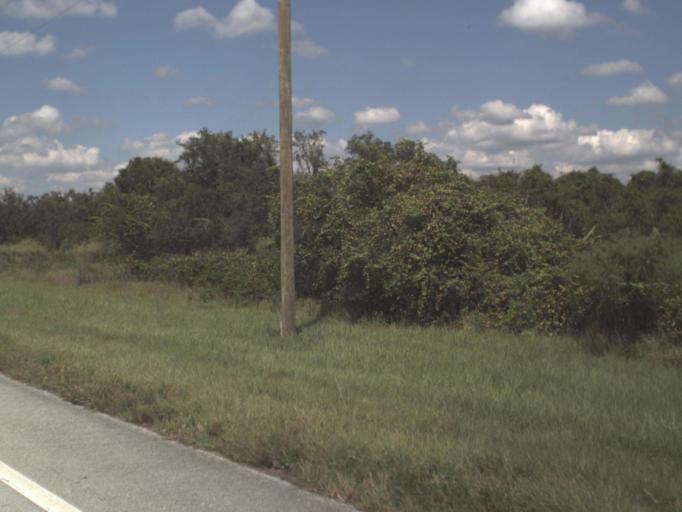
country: US
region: Florida
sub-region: Highlands County
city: Lake Placid
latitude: 27.3896
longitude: -81.1432
